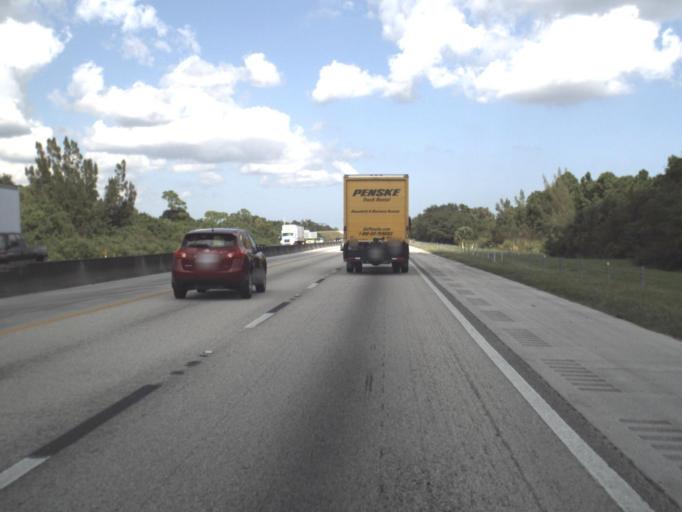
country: US
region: Florida
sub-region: Palm Beach County
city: Palm Beach Gardens
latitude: 26.8588
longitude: -80.1292
